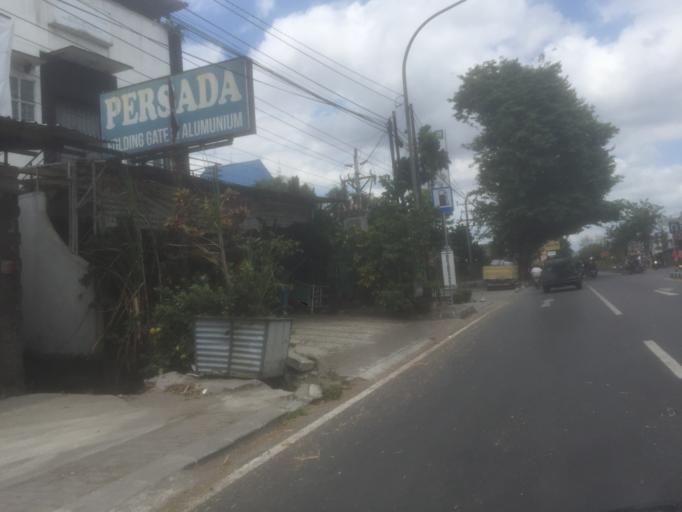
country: ID
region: Daerah Istimewa Yogyakarta
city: Melati
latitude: -7.7315
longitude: 110.3634
